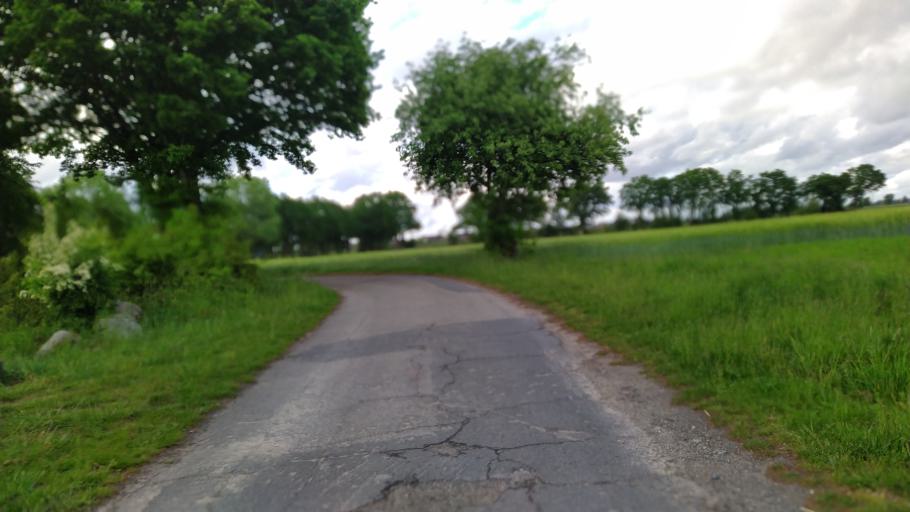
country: DE
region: Lower Saxony
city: Kutenholz
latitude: 53.4694
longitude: 9.3195
